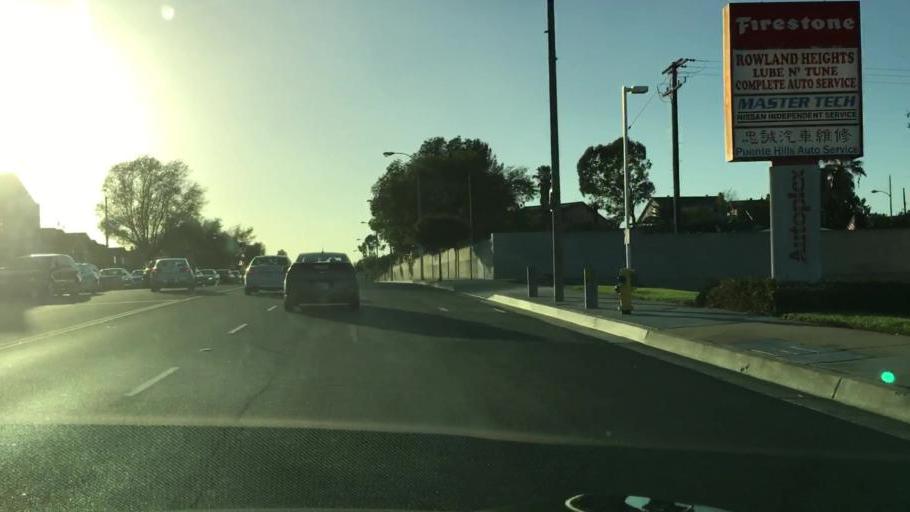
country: US
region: California
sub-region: Los Angeles County
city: Rowland Heights
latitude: 33.9885
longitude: -117.9069
